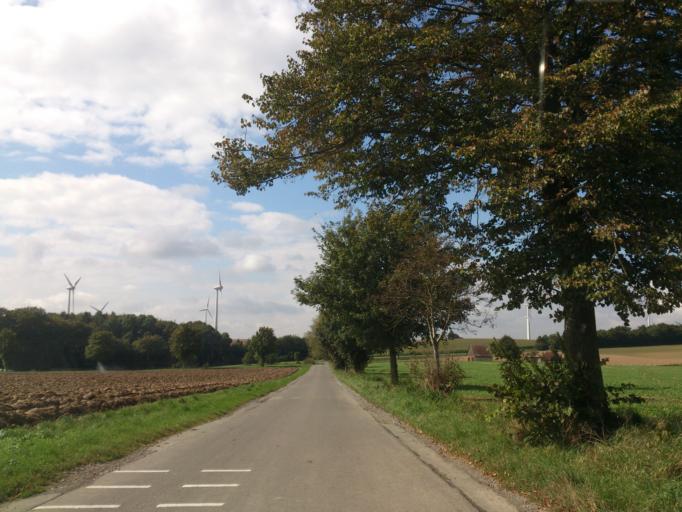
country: DE
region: North Rhine-Westphalia
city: Lichtenau
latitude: 51.6642
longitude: 8.8683
